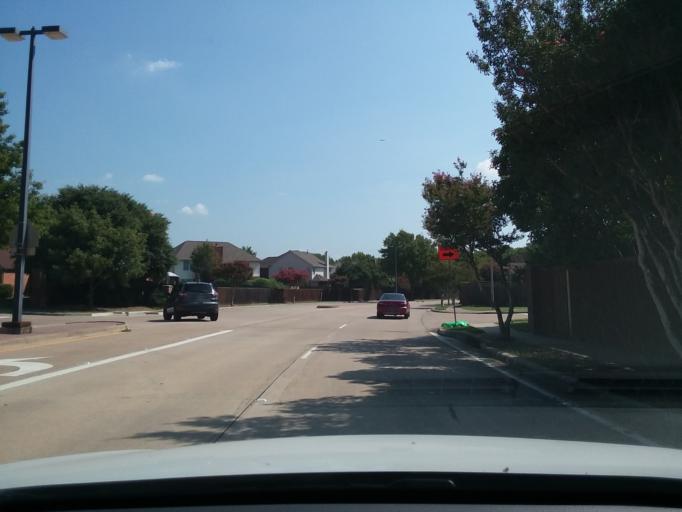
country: US
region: Texas
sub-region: Denton County
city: Flower Mound
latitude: 33.0195
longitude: -97.0540
